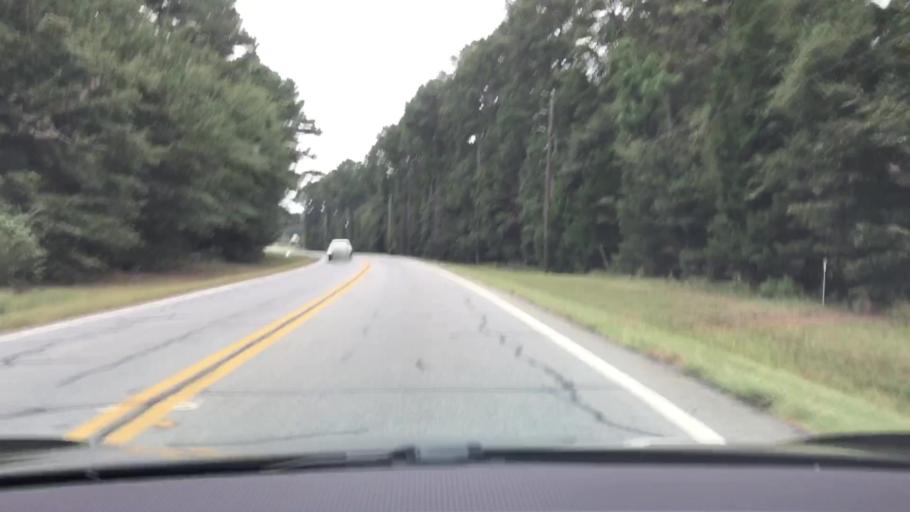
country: US
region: Georgia
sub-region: Oconee County
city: Watkinsville
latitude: 33.7818
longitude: -83.3124
